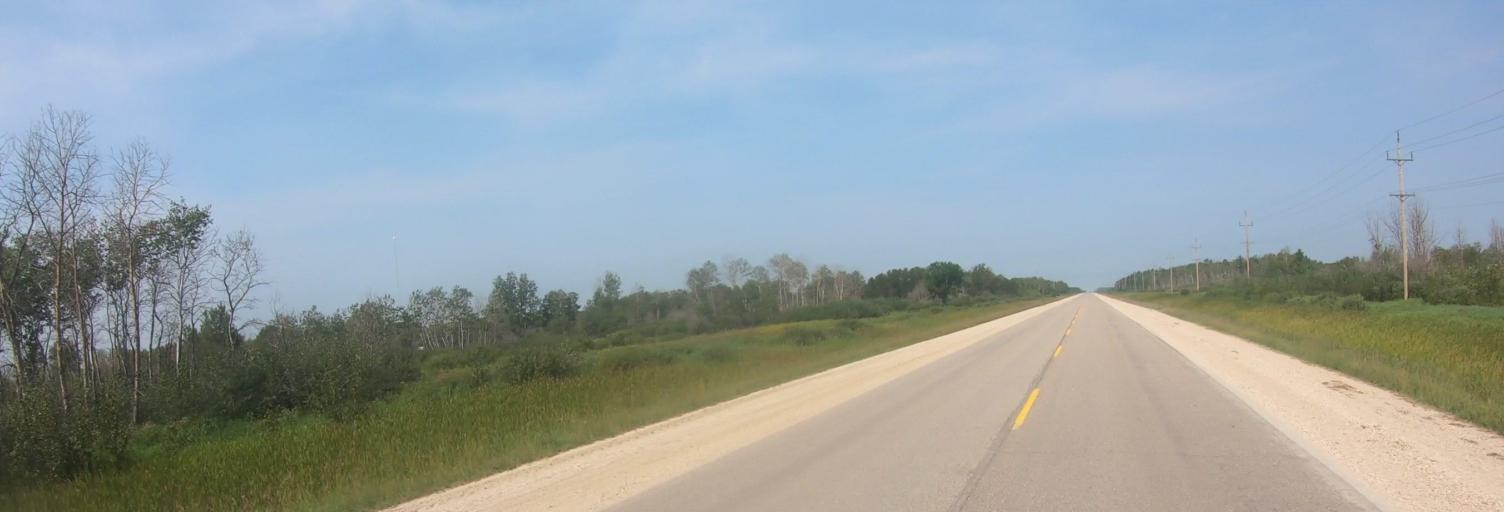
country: CA
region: Manitoba
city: La Broquerie
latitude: 49.2906
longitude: -96.5245
